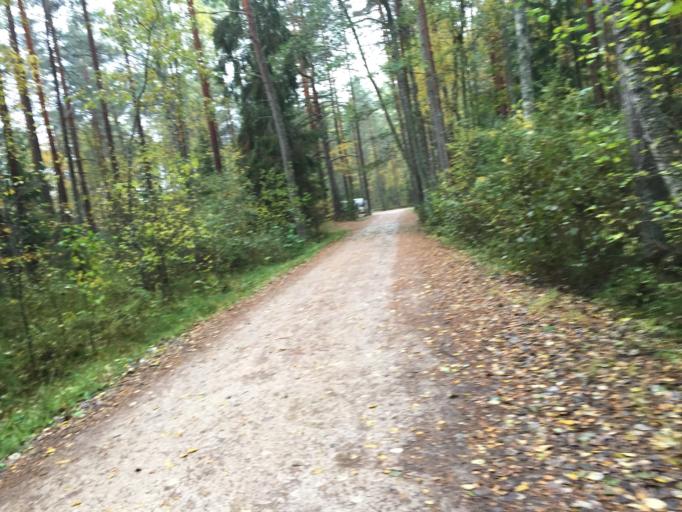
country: LV
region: Engure
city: Smarde
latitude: 56.9138
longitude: 23.4611
